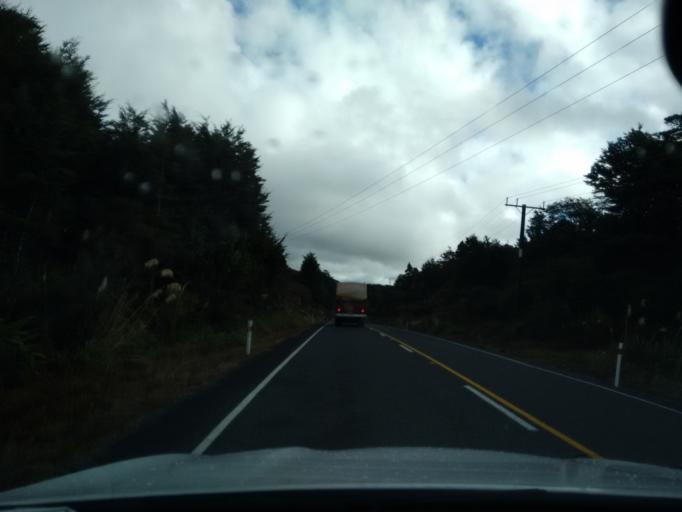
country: NZ
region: Manawatu-Wanganui
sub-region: Ruapehu District
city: Waiouru
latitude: -39.1735
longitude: 175.4745
